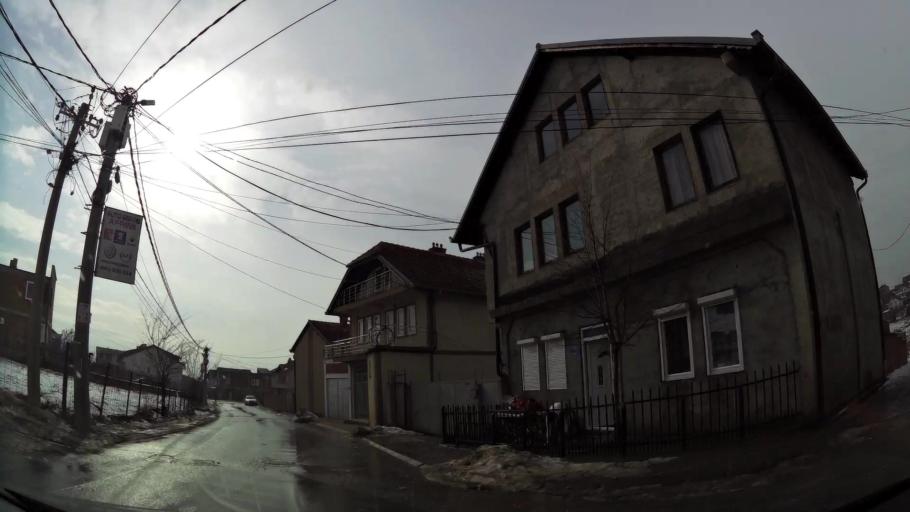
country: XK
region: Pristina
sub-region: Komuna e Prishtines
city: Pristina
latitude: 42.6864
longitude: 21.1647
